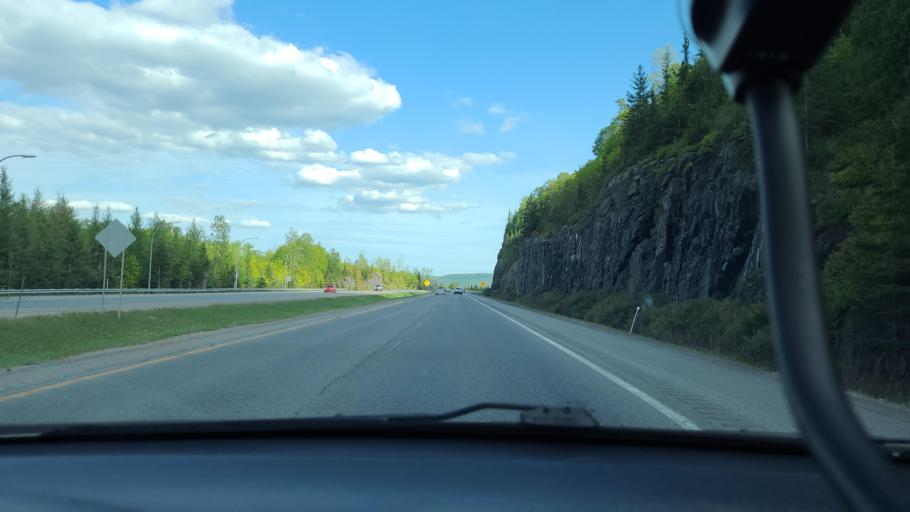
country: CA
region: Quebec
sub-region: Laurentides
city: Sainte-Adele
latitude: 45.9734
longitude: -74.1571
